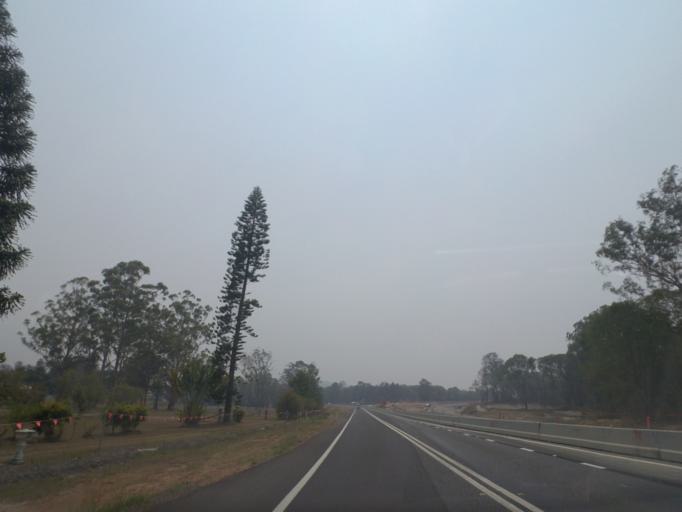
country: AU
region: New South Wales
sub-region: Clarence Valley
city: Maclean
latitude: -29.5515
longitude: 153.1546
